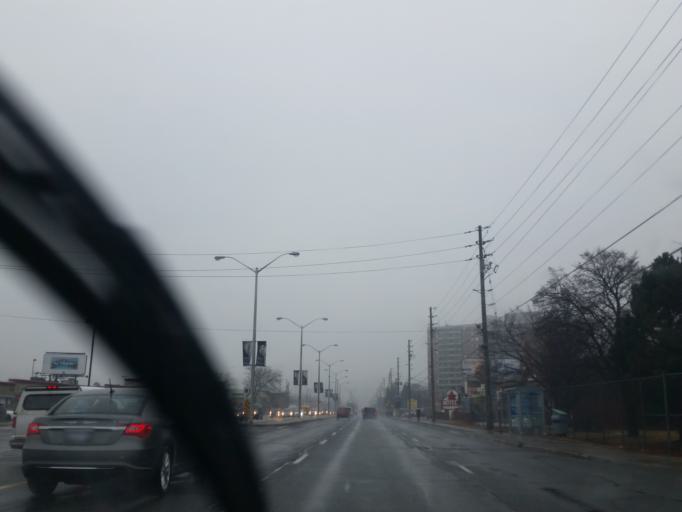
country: CA
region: Ontario
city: Scarborough
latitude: 43.7730
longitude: -79.1849
